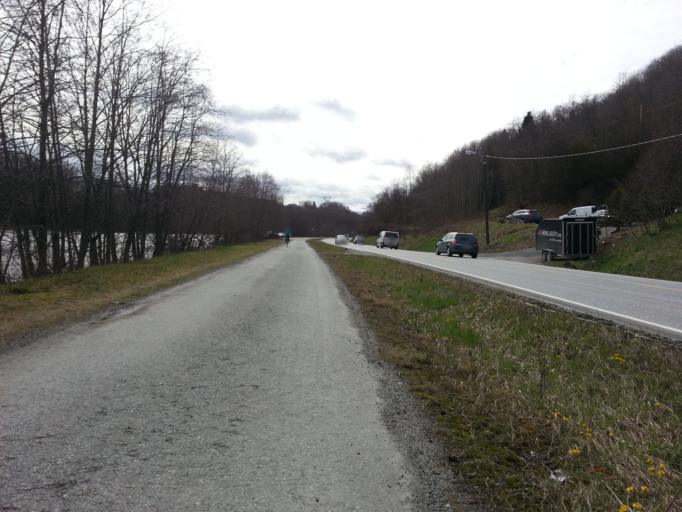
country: NO
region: Sor-Trondelag
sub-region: Trondheim
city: Trondheim
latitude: 63.4015
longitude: 10.3884
